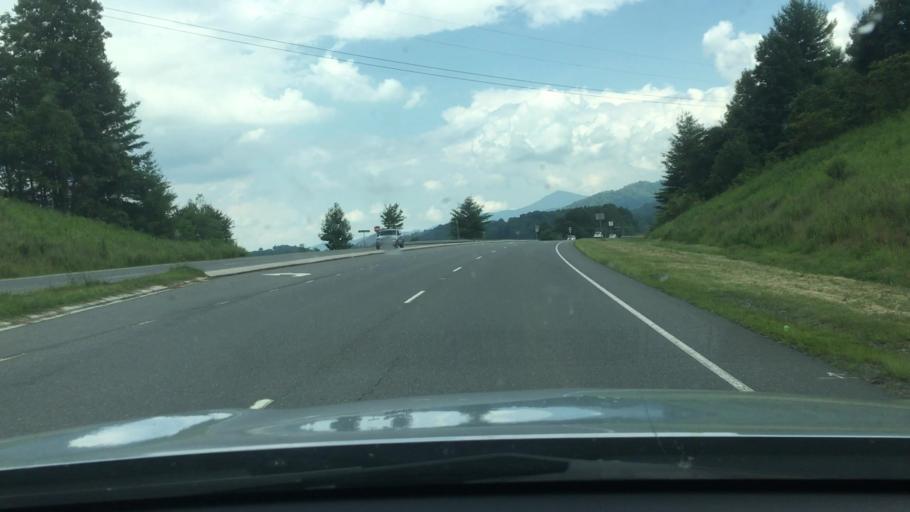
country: US
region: North Carolina
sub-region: Yancey County
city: Burnsville
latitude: 35.9130
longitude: -82.3938
